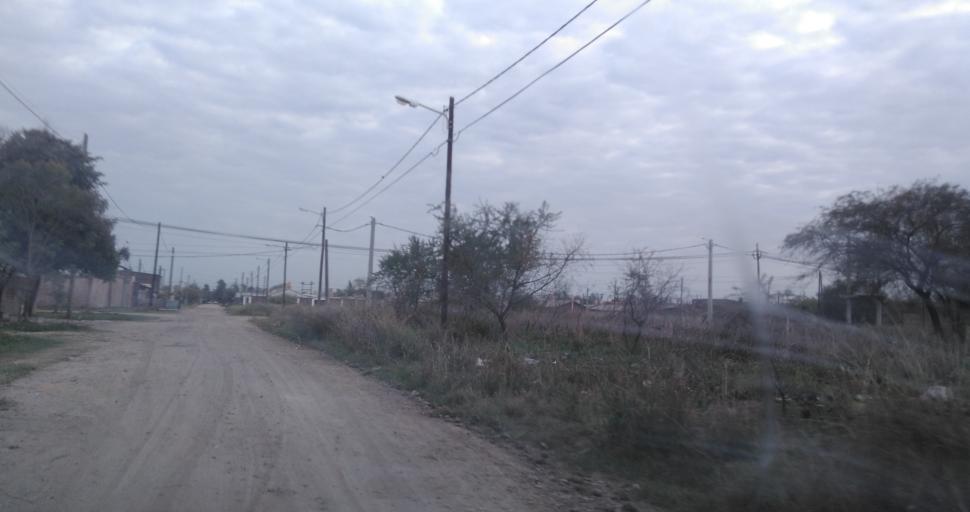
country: AR
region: Chaco
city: Fontana
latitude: -27.4509
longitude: -59.0318
